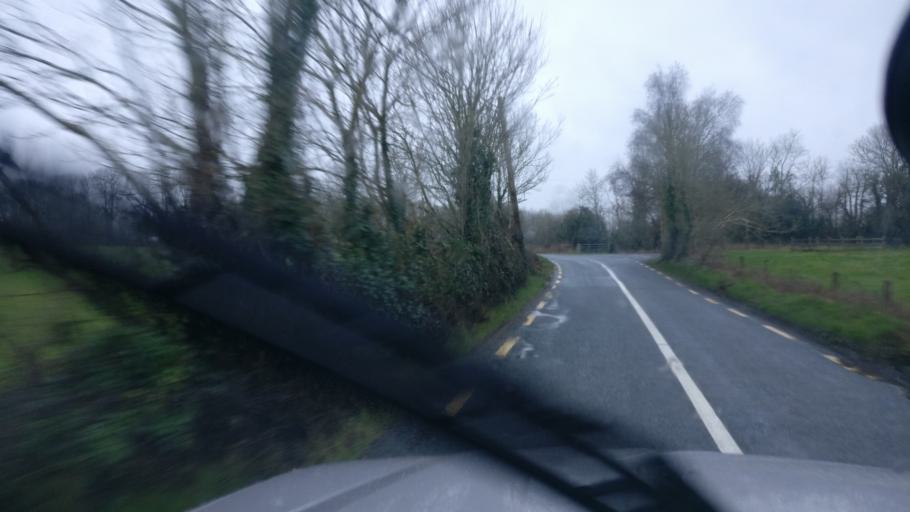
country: IE
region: Connaught
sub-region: County Galway
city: Ballinasloe
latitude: 53.2257
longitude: -8.1940
